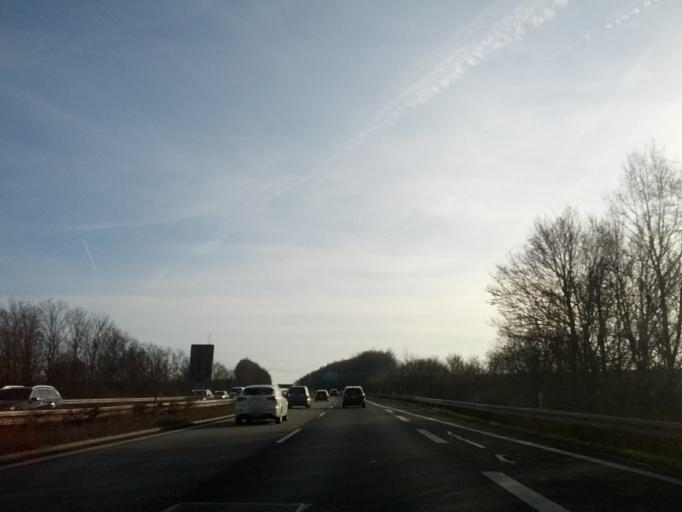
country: DE
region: Bavaria
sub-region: Regierungsbezirk Unterfranken
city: Rottendorf
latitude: 49.7988
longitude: 10.0510
